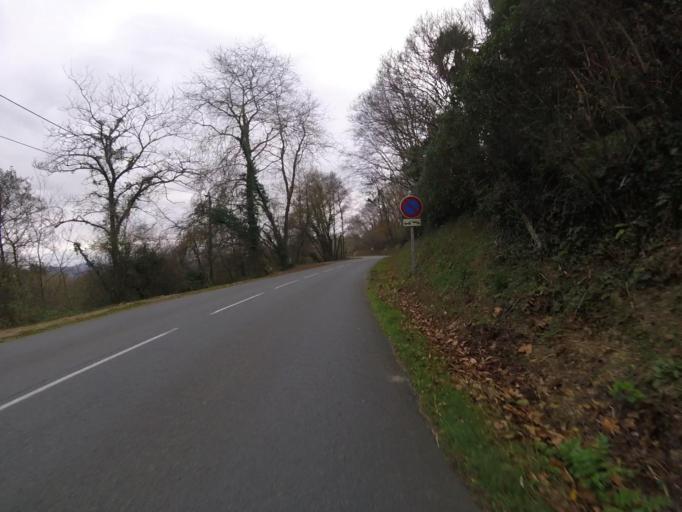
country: FR
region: Aquitaine
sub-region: Departement des Pyrenees-Atlantiques
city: Sare
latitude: 43.3238
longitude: -1.6004
